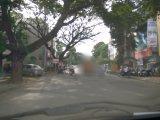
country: IN
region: Karnataka
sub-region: Bangalore Urban
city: Bangalore
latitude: 12.9856
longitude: 77.5426
